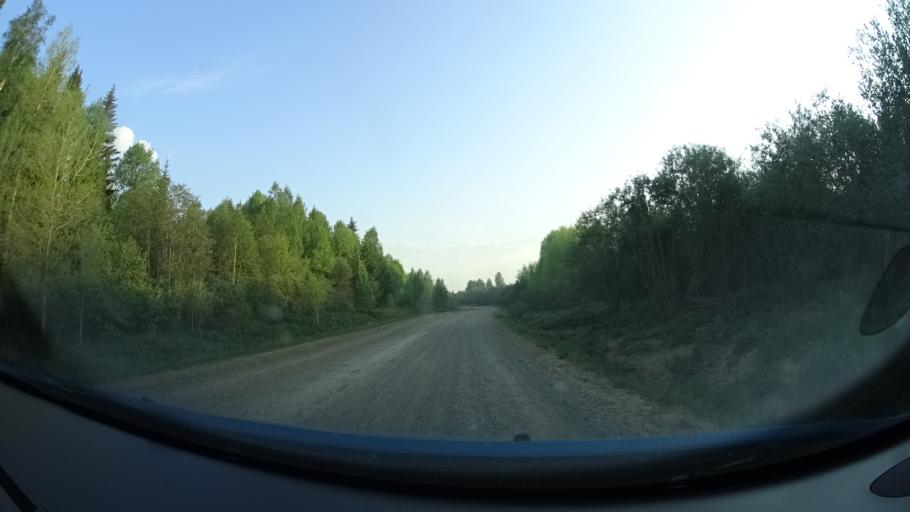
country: RU
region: Perm
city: Kuyeda
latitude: 56.6304
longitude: 55.7105
